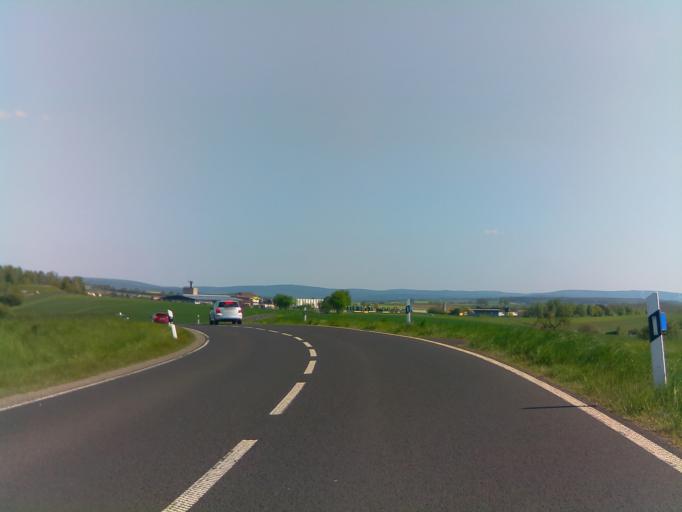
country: DE
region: Hesse
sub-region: Regierungsbezirk Darmstadt
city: Birstein
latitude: 50.3695
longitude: 9.3037
